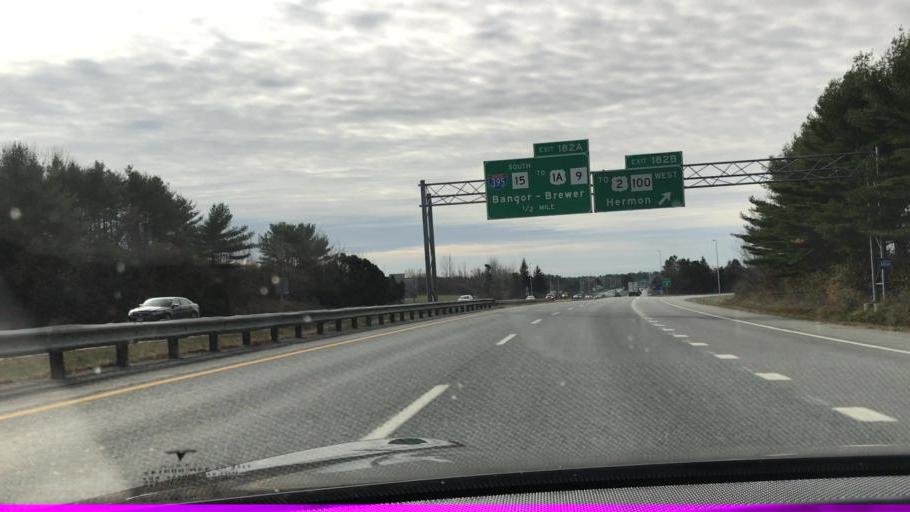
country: US
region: Maine
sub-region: Penobscot County
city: Bangor
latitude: 44.7934
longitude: -68.8040
